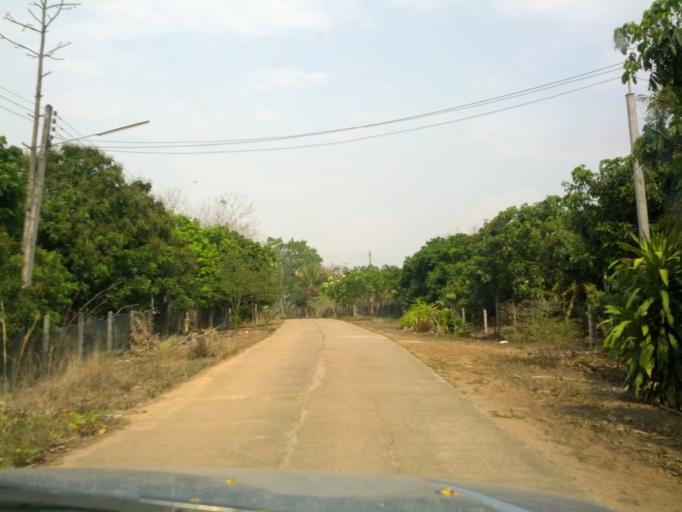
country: TH
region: Chiang Mai
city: Mae Taeng
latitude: 19.1143
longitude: 98.9988
